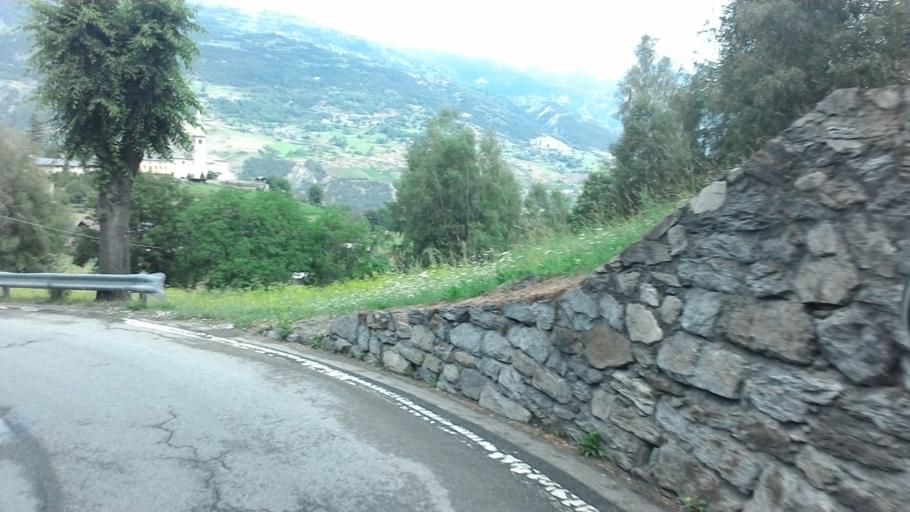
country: IT
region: Aosta Valley
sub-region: Valle d'Aosta
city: Plan d'Introd
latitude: 45.6877
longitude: 7.1882
